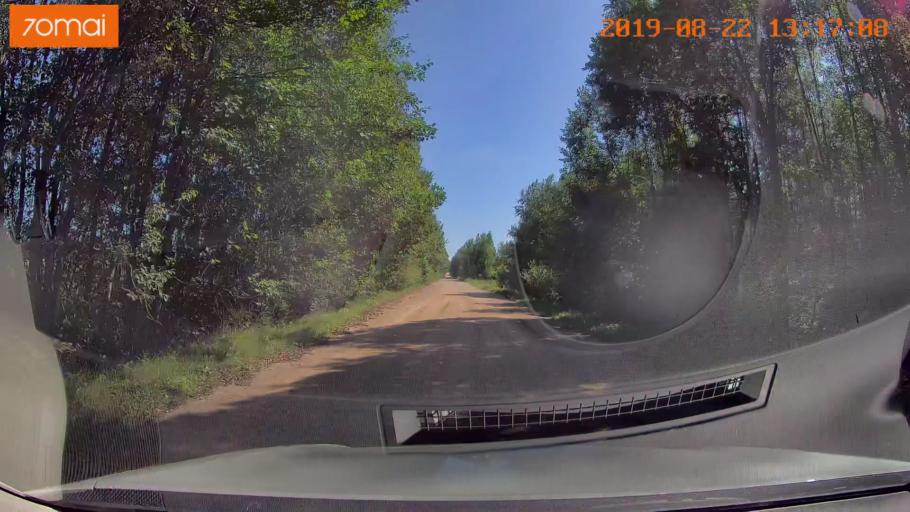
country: BY
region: Minsk
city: Prawdzinski
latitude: 53.2504
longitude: 27.9177
